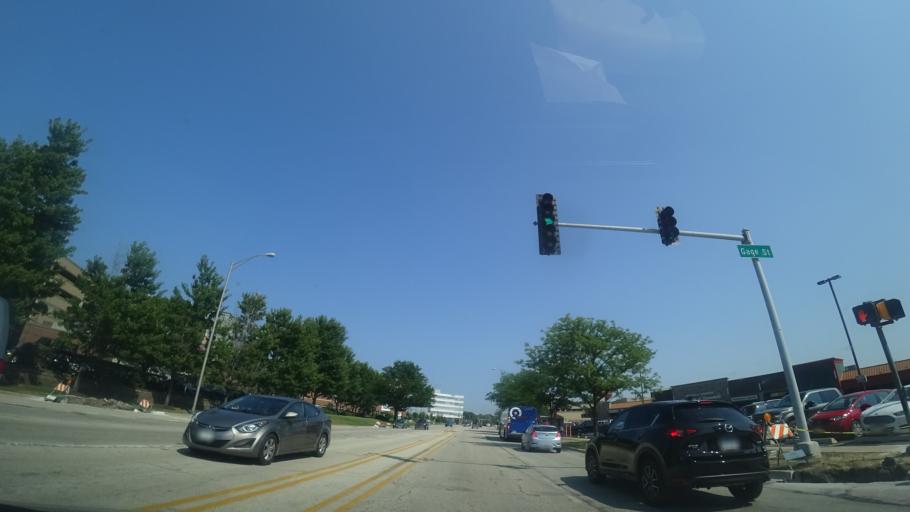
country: US
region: Illinois
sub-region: Cook County
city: Rosemont
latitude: 41.9929
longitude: -87.8647
